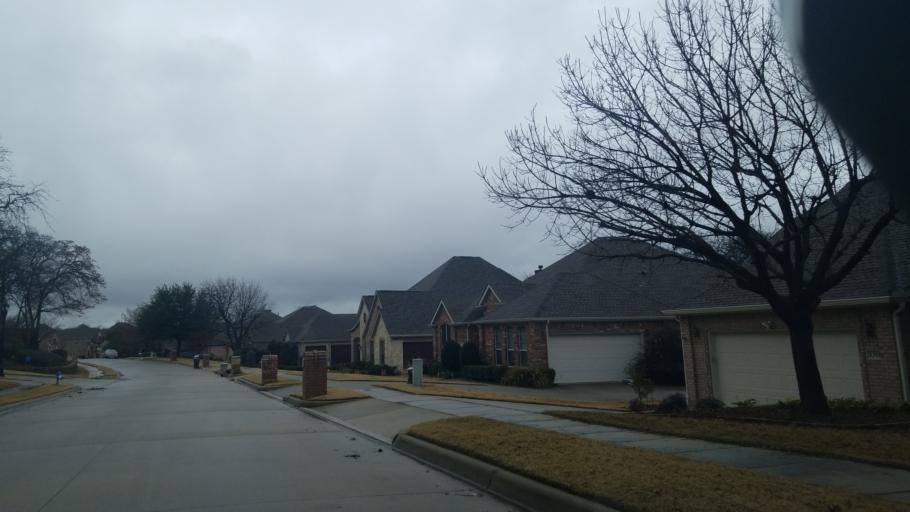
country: US
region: Texas
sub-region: Denton County
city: Corinth
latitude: 33.1462
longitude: -97.0874
